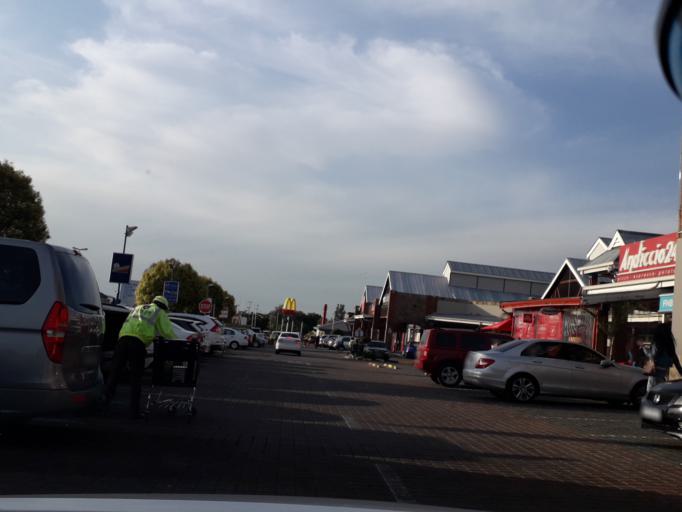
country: ZA
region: Gauteng
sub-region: City of Johannesburg Metropolitan Municipality
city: Johannesburg
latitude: -26.0948
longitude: 27.9851
